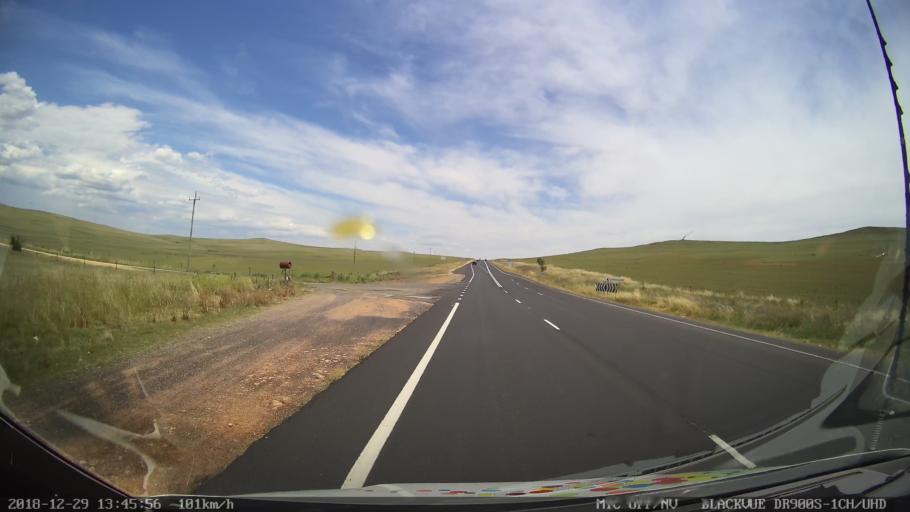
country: AU
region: New South Wales
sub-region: Cooma-Monaro
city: Cooma
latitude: -36.1043
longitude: 149.1445
